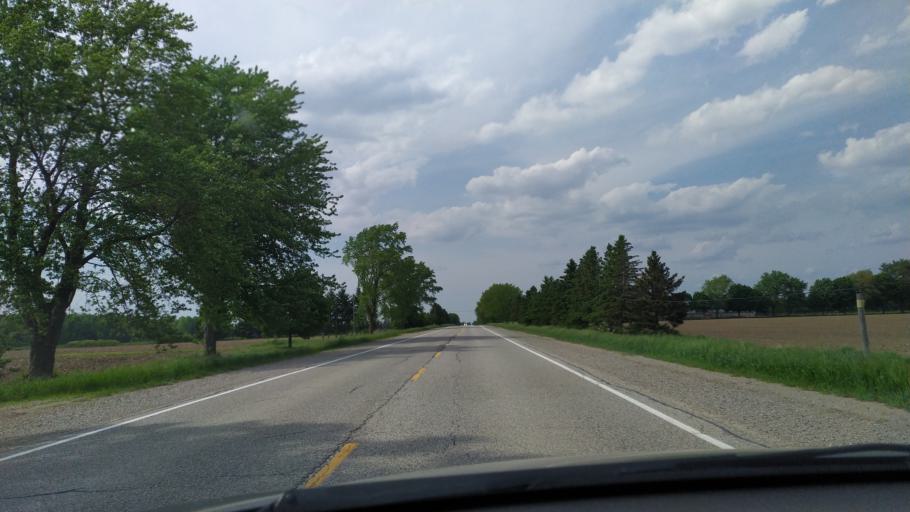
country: CA
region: Ontario
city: Dorchester
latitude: 43.1164
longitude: -81.0186
